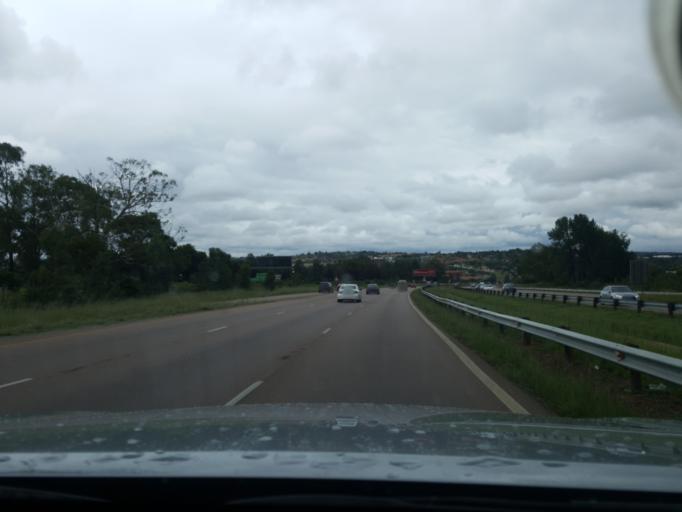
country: ZA
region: Gauteng
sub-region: City of Tshwane Metropolitan Municipality
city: Centurion
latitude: -25.8400
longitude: 28.1836
